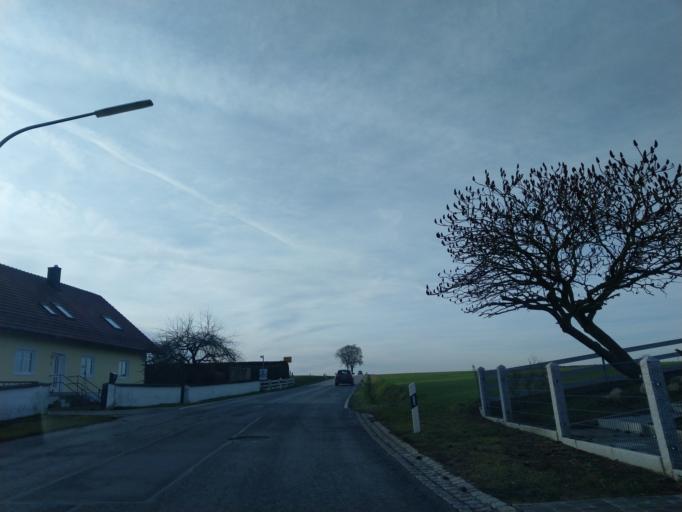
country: DE
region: Bavaria
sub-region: Lower Bavaria
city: Buchhofen
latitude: 48.7011
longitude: 12.9680
